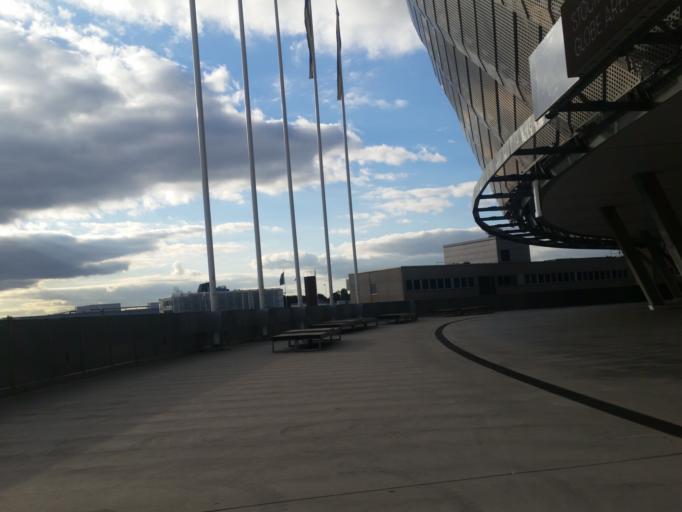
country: SE
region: Stockholm
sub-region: Stockholms Kommun
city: Arsta
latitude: 59.2902
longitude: 18.0847
